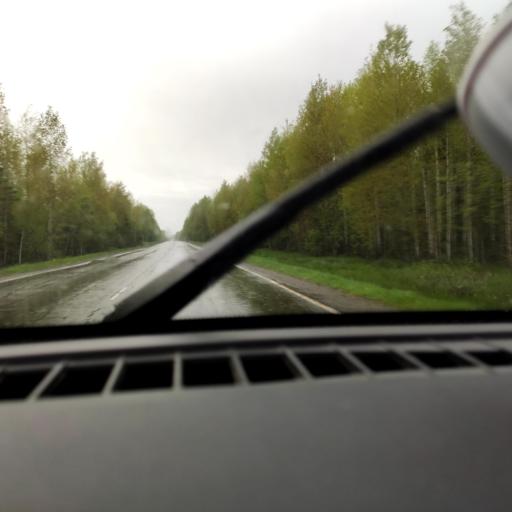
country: RU
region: Perm
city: Polazna
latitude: 58.2685
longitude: 56.1675
